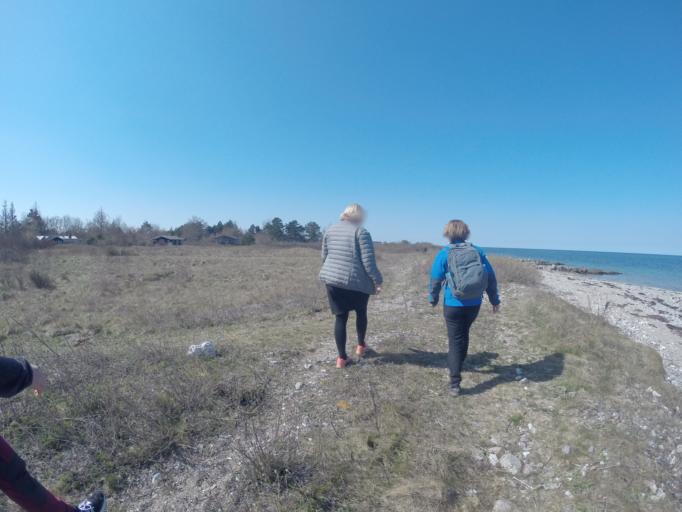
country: DK
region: Zealand
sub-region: Kalundborg Kommune
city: Gorlev
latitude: 55.5368
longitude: 11.1184
